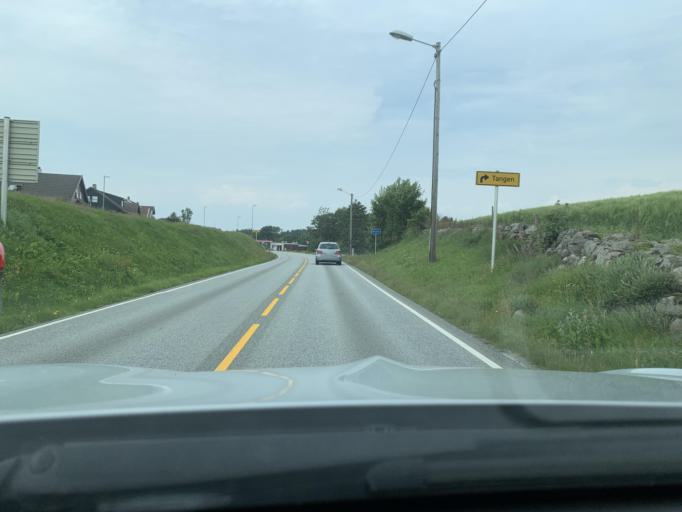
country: NO
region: Rogaland
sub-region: Time
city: Bryne
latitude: 58.7346
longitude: 5.6723
